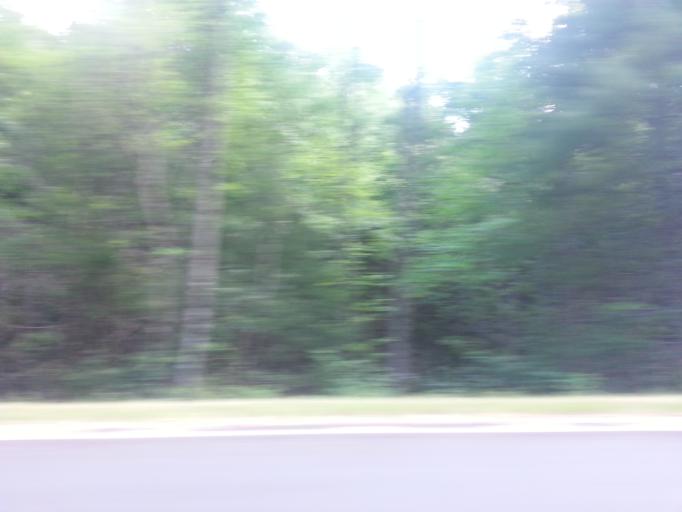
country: US
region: Georgia
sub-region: Towns County
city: Hiawassee
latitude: 34.8320
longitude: -83.7629
